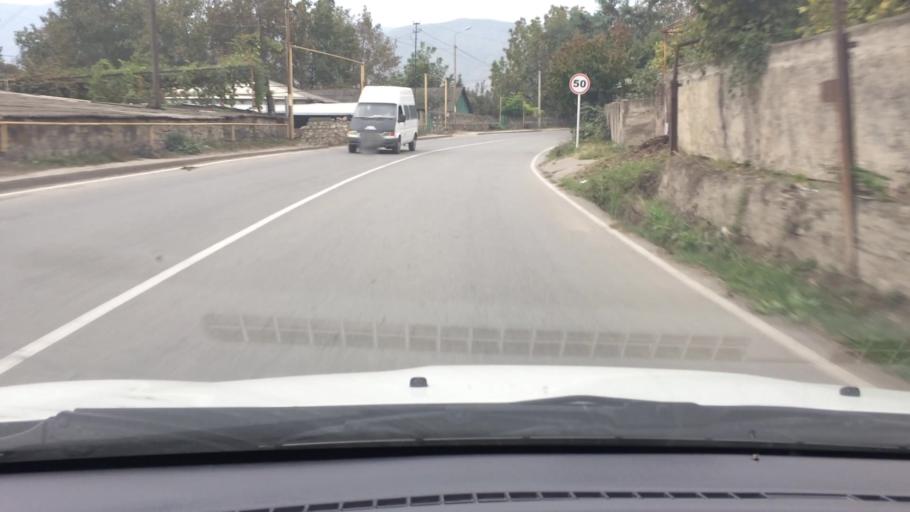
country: AM
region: Tavush
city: Bagratashen
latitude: 41.2488
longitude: 44.7999
